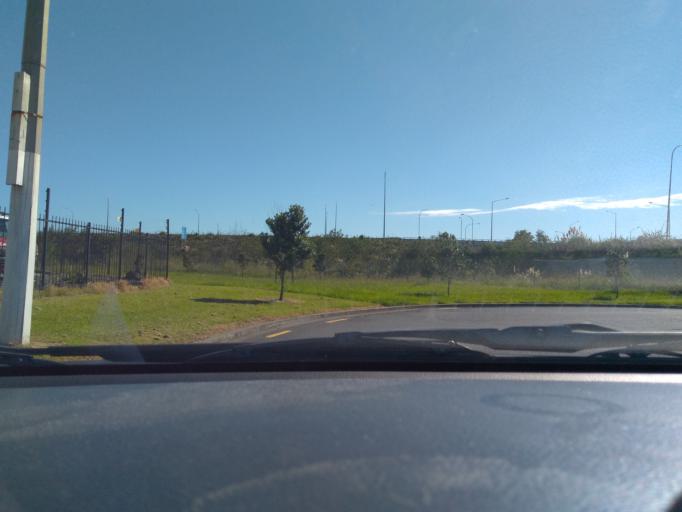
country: NZ
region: Auckland
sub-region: Auckland
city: Wiri
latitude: -36.9992
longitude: 174.8508
